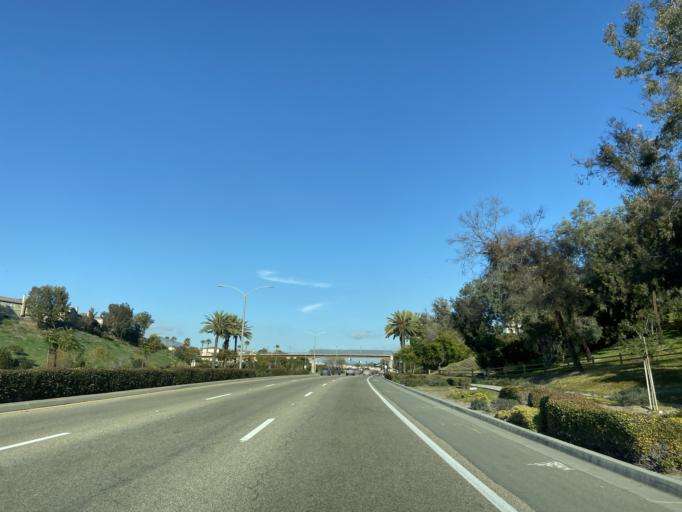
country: US
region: California
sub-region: San Diego County
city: Bonita
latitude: 32.6276
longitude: -116.9820
